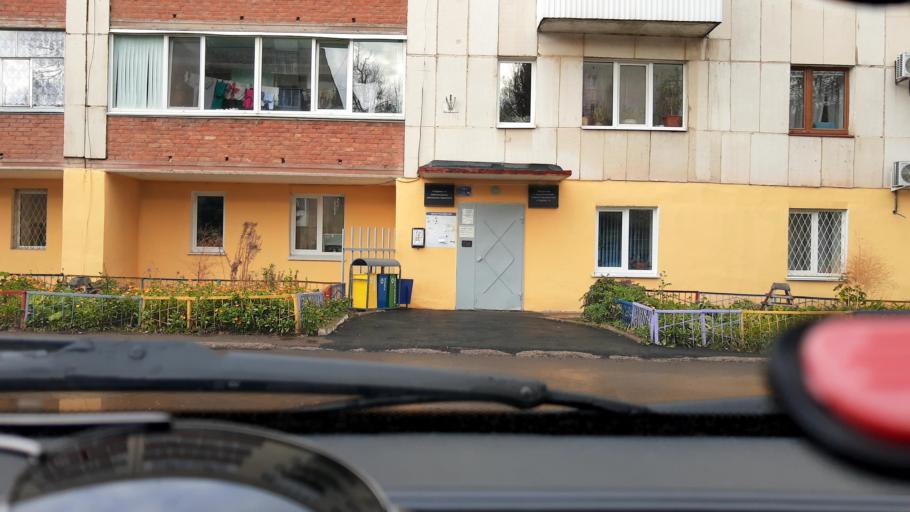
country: RU
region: Bashkortostan
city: Ufa
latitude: 54.7609
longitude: 56.0049
